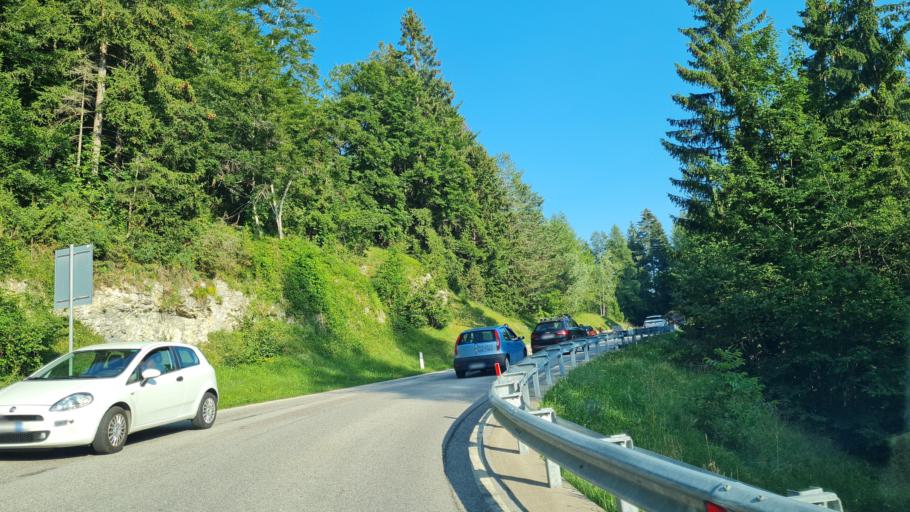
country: IT
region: Trentino-Alto Adige
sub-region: Provincia di Trento
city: Gionghi-Cappella
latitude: 45.9380
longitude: 11.2855
